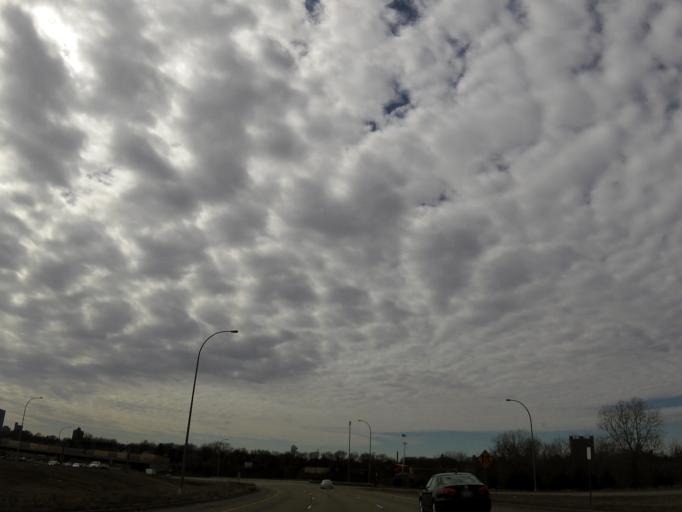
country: US
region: Minnesota
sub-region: Hennepin County
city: Saint Anthony
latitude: 45.0027
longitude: -93.2327
